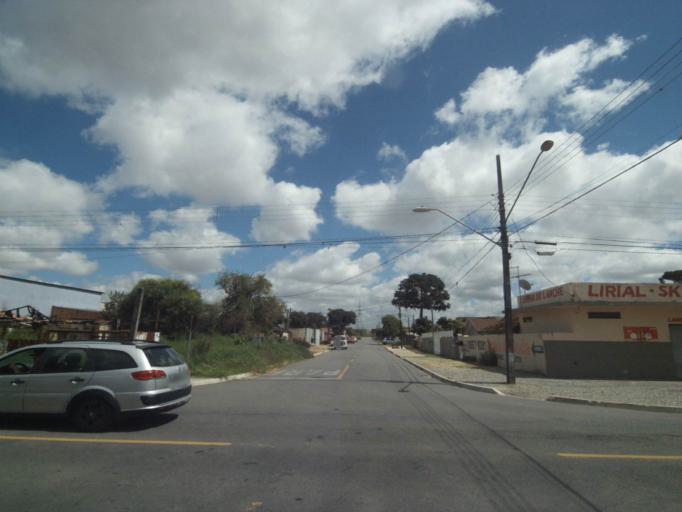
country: BR
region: Parana
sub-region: Pinhais
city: Pinhais
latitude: -25.4427
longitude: -49.1987
